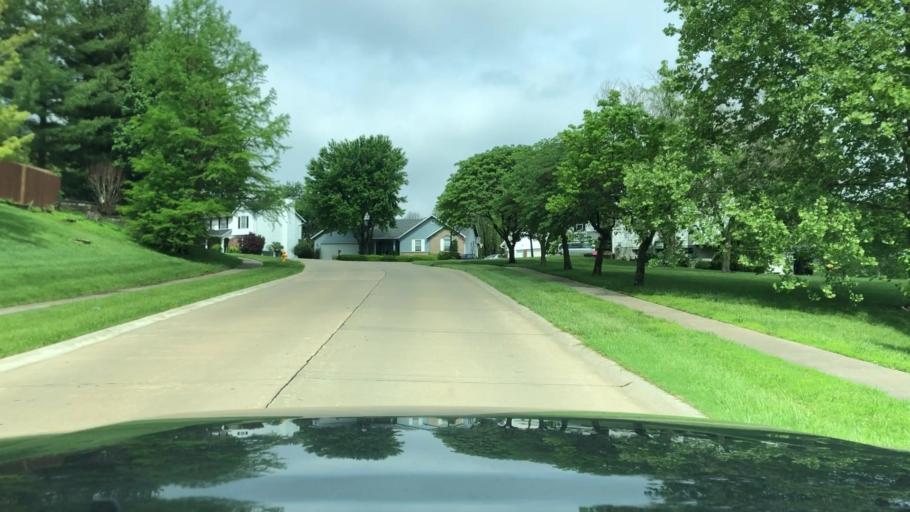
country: US
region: Missouri
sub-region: Saint Charles County
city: Saint Charles
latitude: 38.8076
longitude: -90.5120
